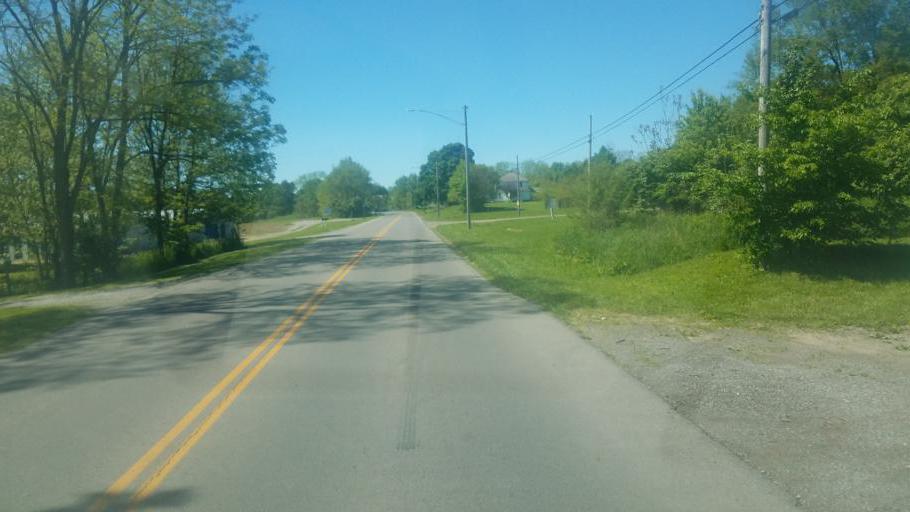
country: US
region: Ohio
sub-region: Logan County
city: Bellefontaine
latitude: 40.3690
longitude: -83.7759
